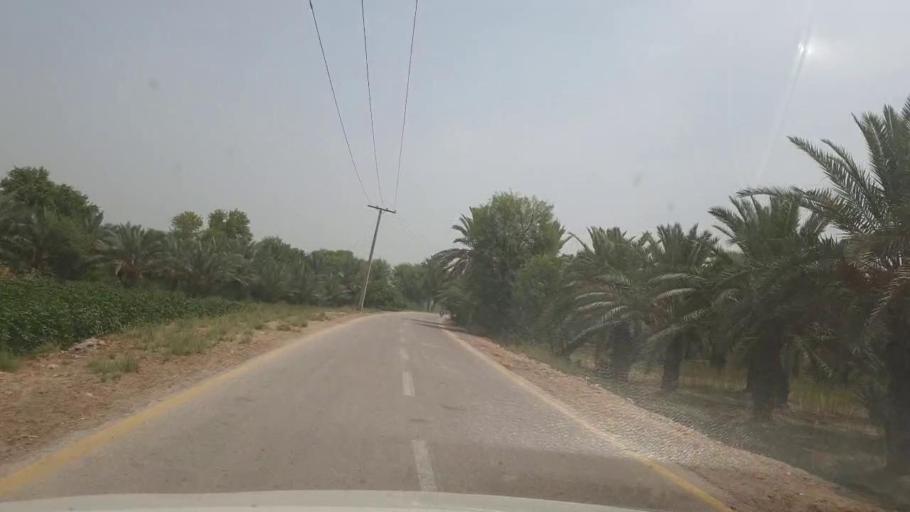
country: PK
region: Sindh
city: Kot Diji
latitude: 27.3674
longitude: 68.6440
